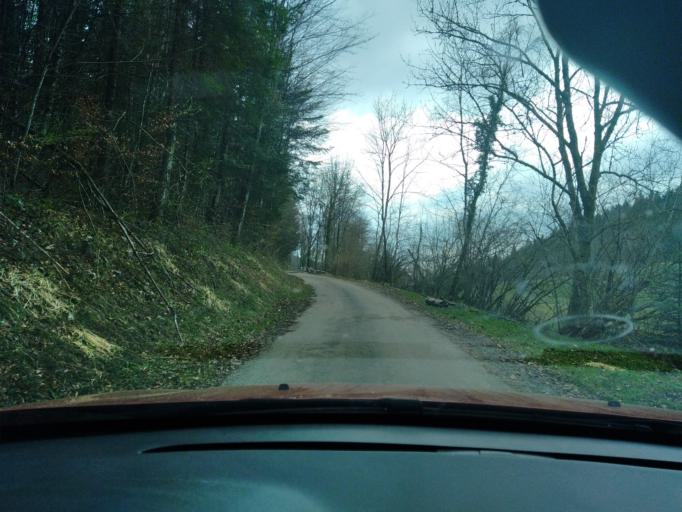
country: FR
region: Franche-Comte
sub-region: Departement du Jura
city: Moirans-en-Montagne
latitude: 46.4601
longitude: 5.7609
